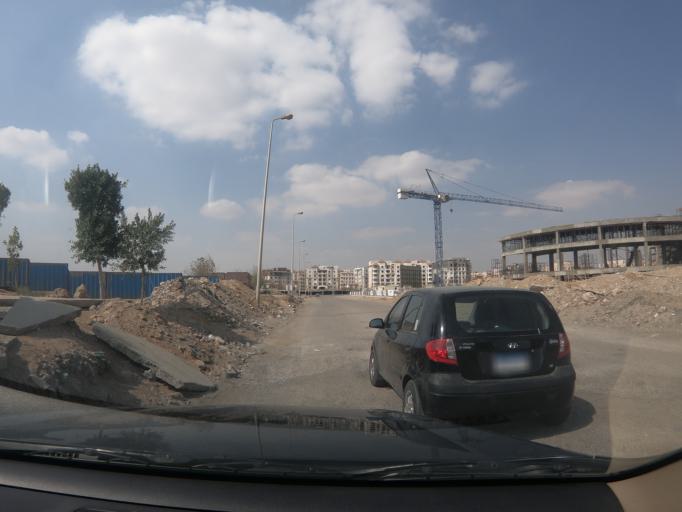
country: EG
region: Muhafazat al Qalyubiyah
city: Al Khankah
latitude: 30.0266
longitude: 31.4764
